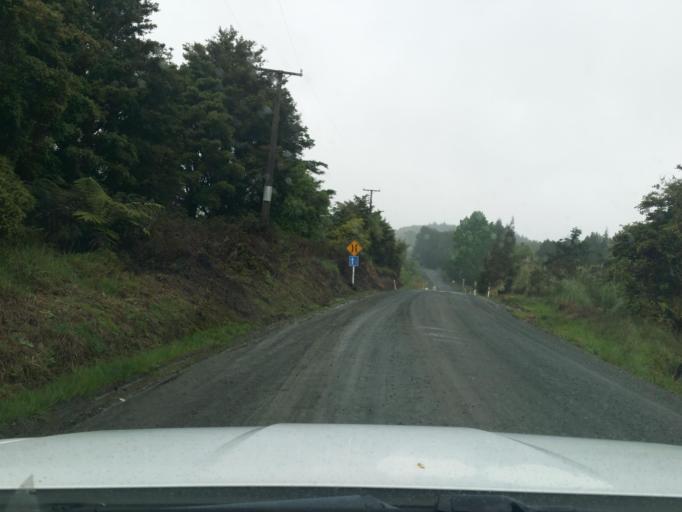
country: NZ
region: Northland
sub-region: Kaipara District
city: Dargaville
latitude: -35.7401
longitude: 173.9081
